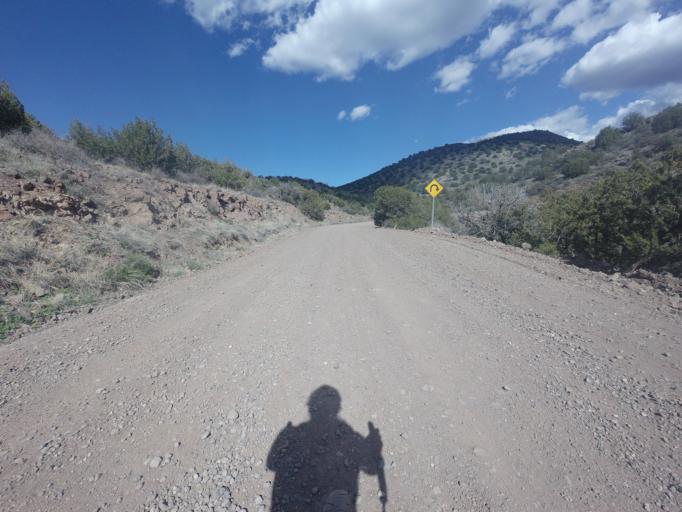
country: US
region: Arizona
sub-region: Yavapai County
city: Camp Verde
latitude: 34.4587
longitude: -111.7108
